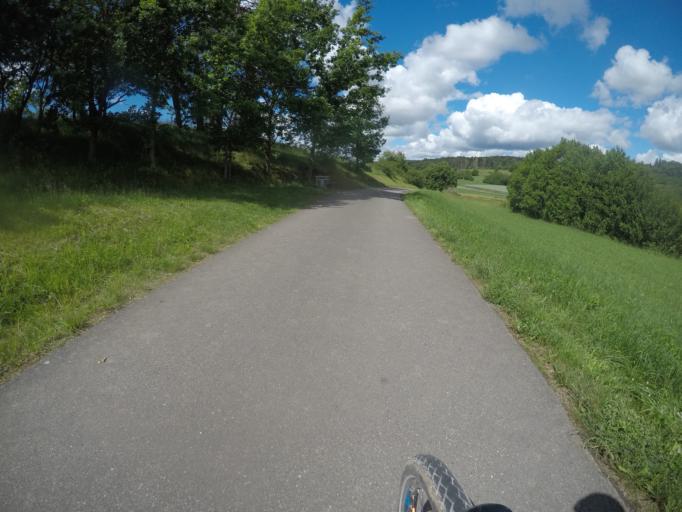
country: DE
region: Baden-Wuerttemberg
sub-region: Karlsruhe Region
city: Horb am Neckar
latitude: 48.4744
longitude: 8.7316
